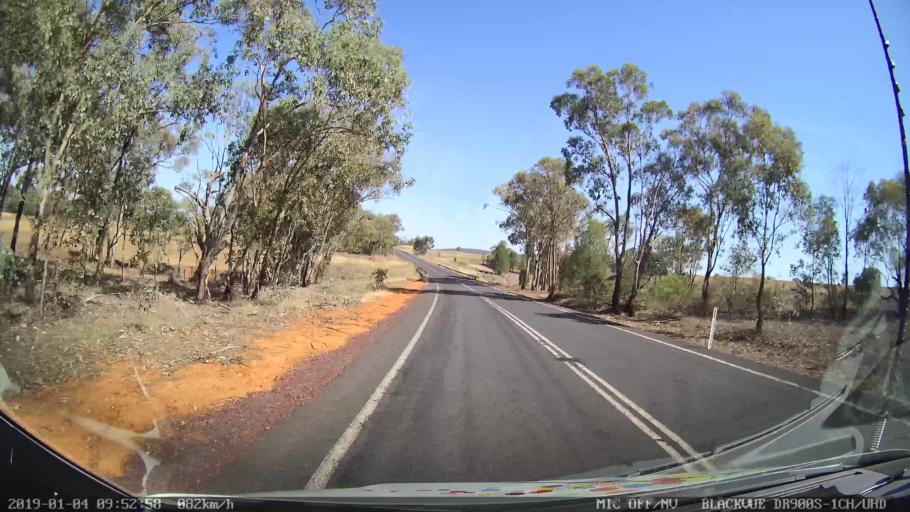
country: AU
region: New South Wales
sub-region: Cabonne
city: Canowindra
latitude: -33.5575
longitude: 148.4239
